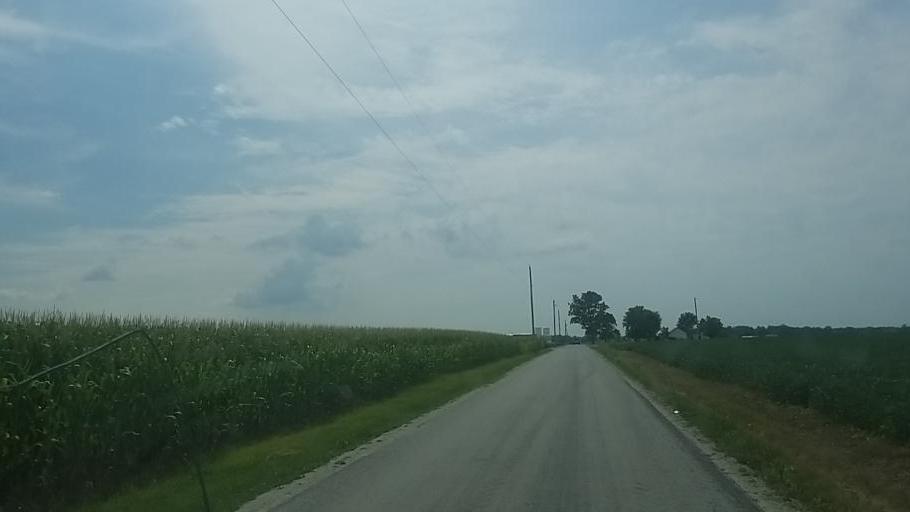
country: US
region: Ohio
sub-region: Hardin County
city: Forest
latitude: 40.7600
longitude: -83.5457
